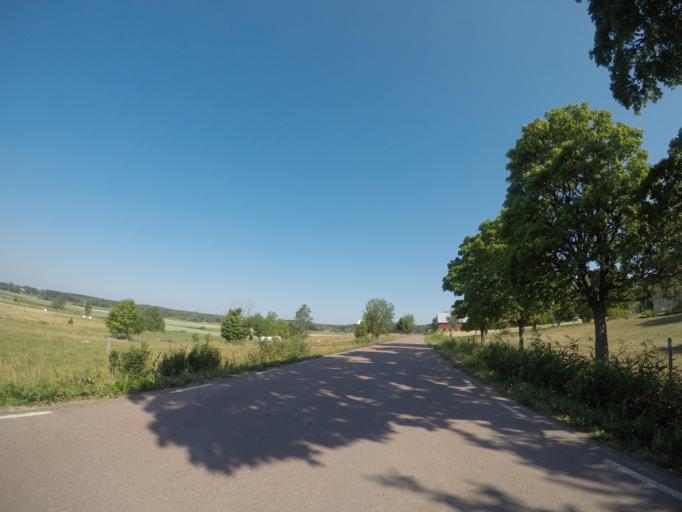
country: AX
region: Alands landsbygd
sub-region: Jomala
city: Jomala
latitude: 60.2047
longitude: 19.9740
